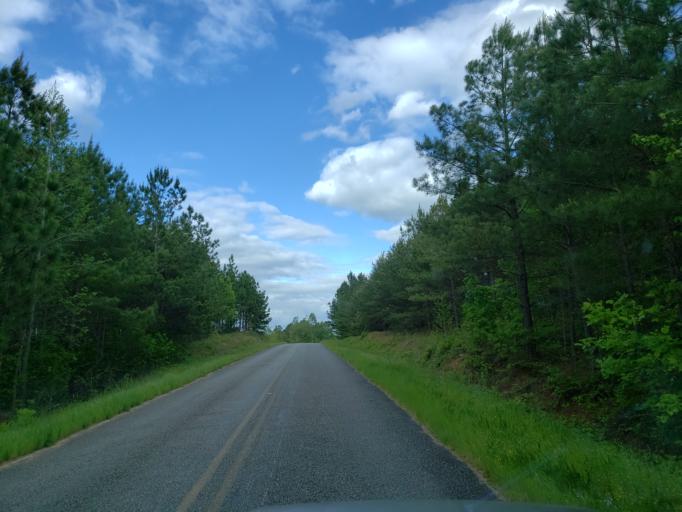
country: US
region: Georgia
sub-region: Haralson County
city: Tallapoosa
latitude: 33.8186
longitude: -85.3791
